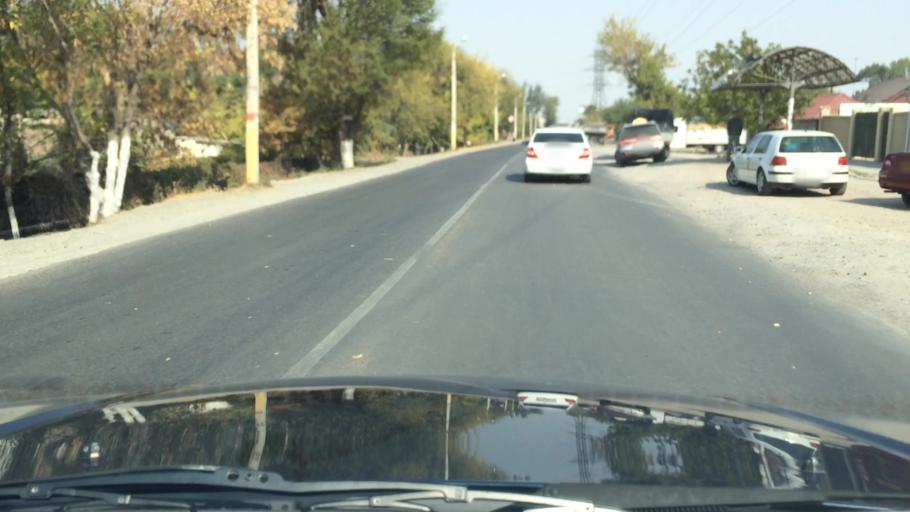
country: KG
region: Chuy
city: Lebedinovka
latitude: 42.8862
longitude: 74.6786
